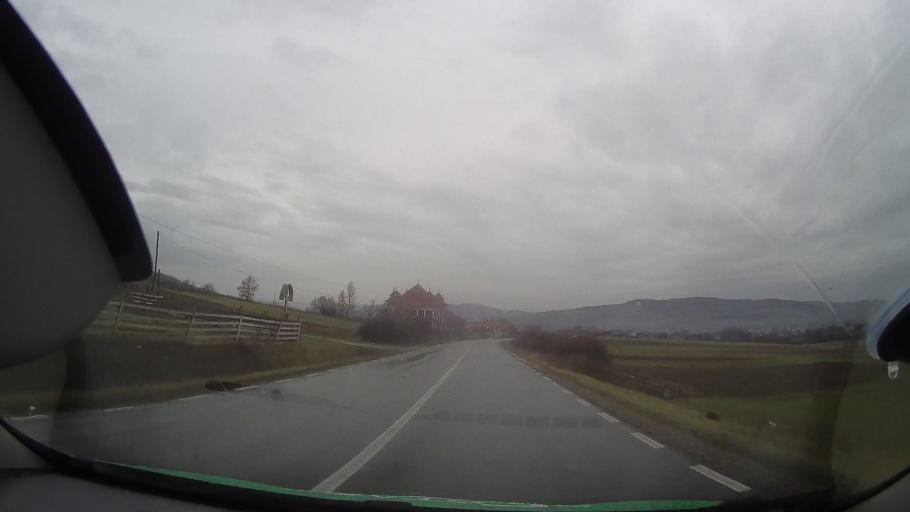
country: RO
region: Bihor
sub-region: Comuna Rabagani
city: Rabagani
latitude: 46.7424
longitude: 22.2282
